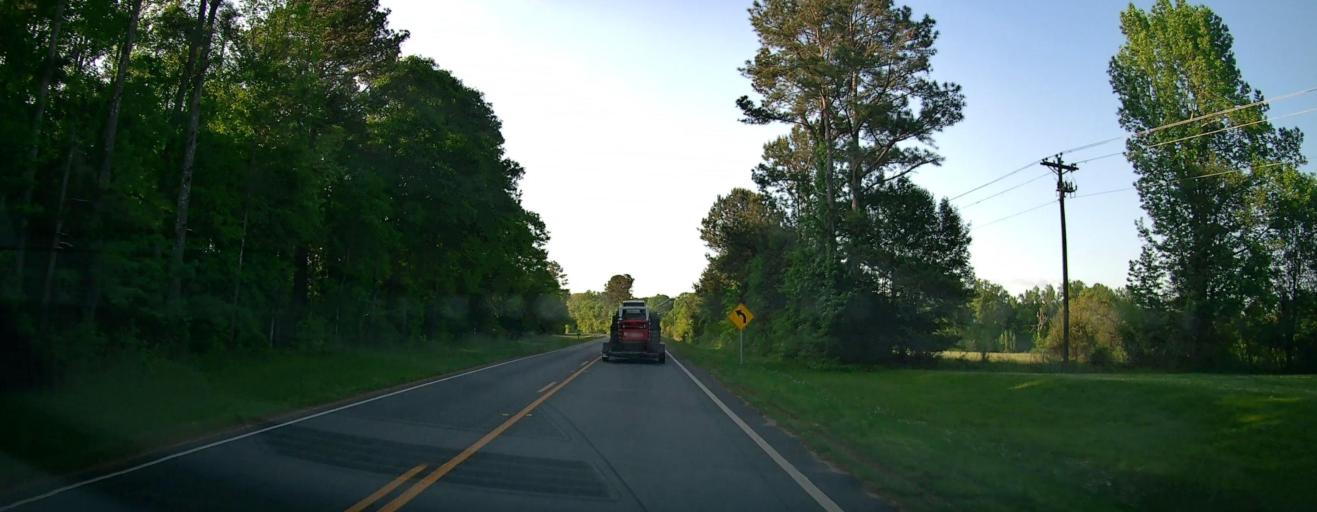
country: US
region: Georgia
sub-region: Putnam County
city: Eatonton
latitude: 33.3480
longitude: -83.5143
